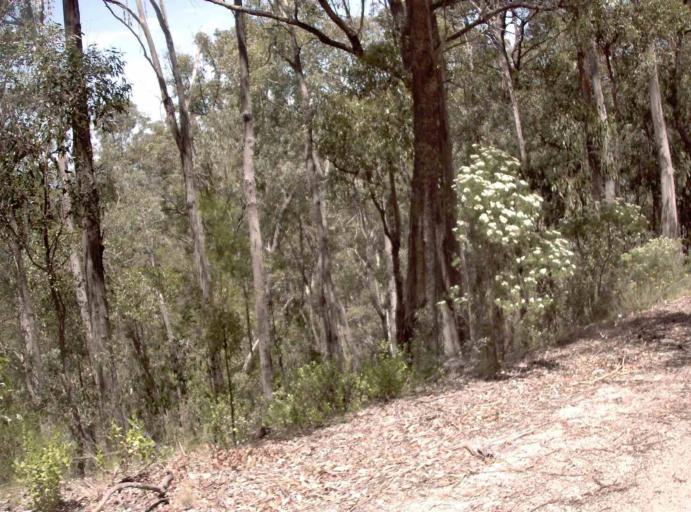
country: AU
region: Victoria
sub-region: East Gippsland
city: Lakes Entrance
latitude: -37.6074
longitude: 147.8824
